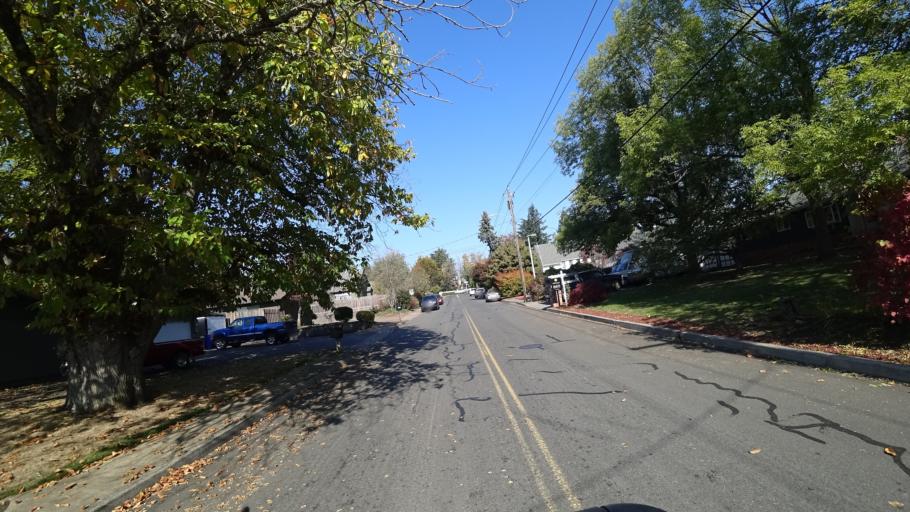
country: US
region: Oregon
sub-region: Multnomah County
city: Gresham
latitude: 45.4956
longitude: -122.4470
